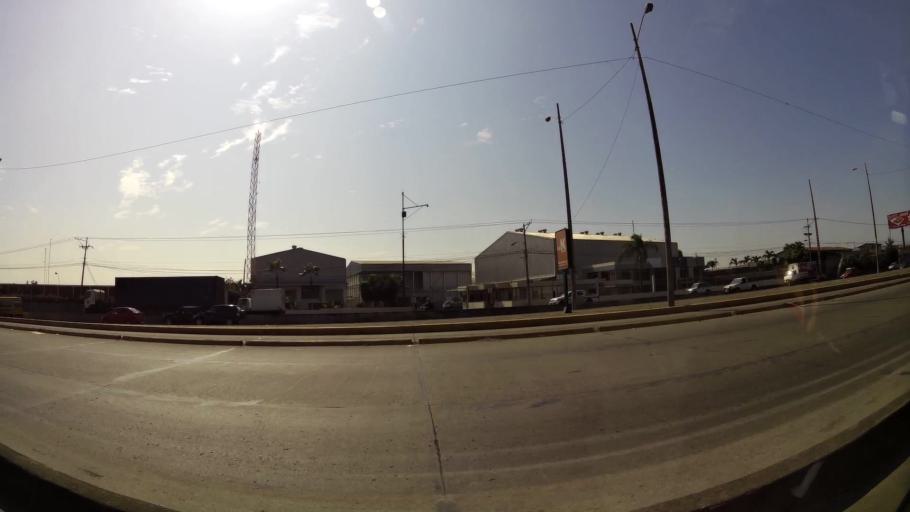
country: EC
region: Guayas
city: Santa Lucia
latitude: -2.1071
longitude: -79.9346
